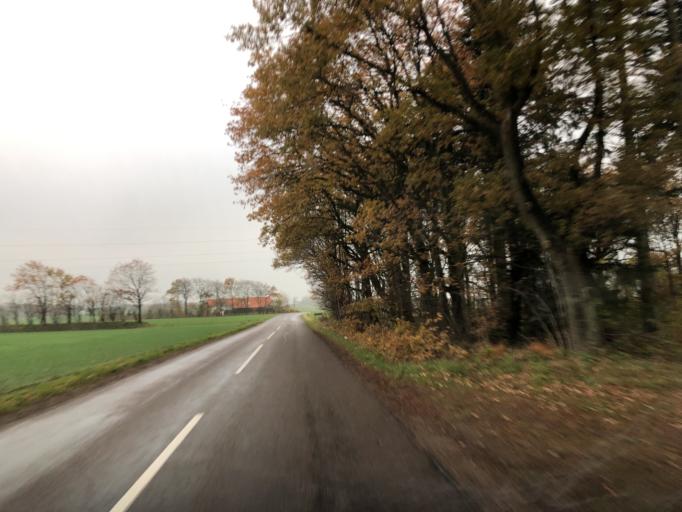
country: DK
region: Central Jutland
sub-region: Herning Kommune
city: Avlum
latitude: 56.2473
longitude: 8.8468
